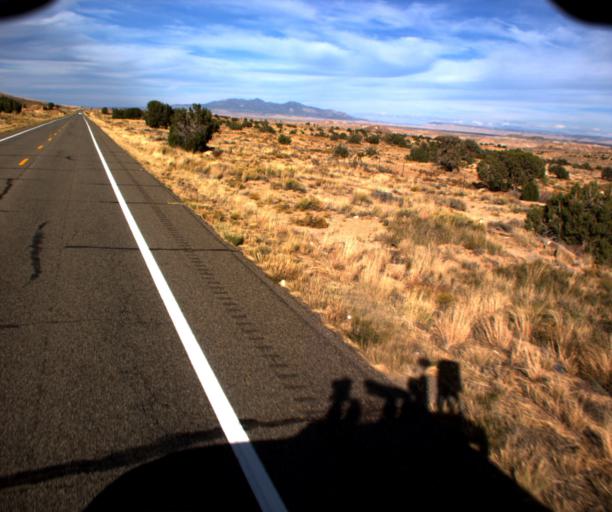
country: US
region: Colorado
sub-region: Montezuma County
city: Towaoc
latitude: 36.9738
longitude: -109.0603
